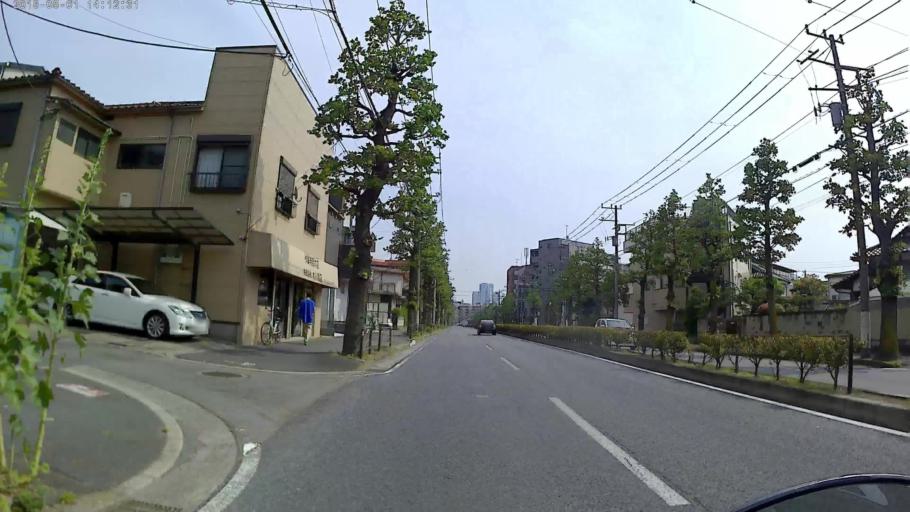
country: JP
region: Kanagawa
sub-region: Kawasaki-shi
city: Kawasaki
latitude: 35.5704
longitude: 139.6697
